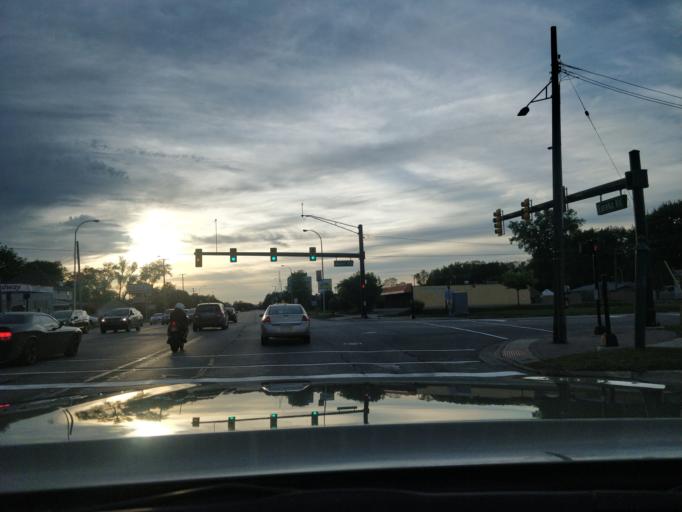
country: US
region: Michigan
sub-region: Wayne County
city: Southgate
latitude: 42.1987
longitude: -83.2283
